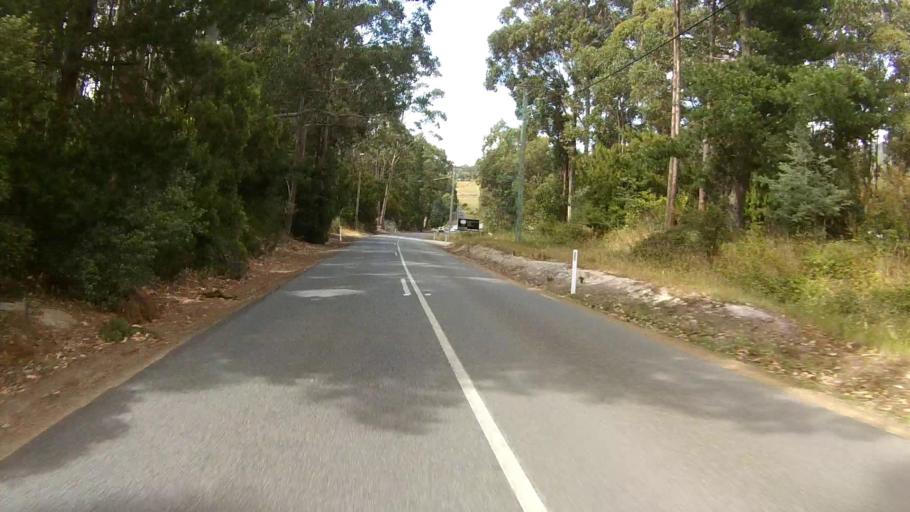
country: AU
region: Tasmania
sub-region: Kingborough
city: Kettering
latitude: -43.1801
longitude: 147.2380
